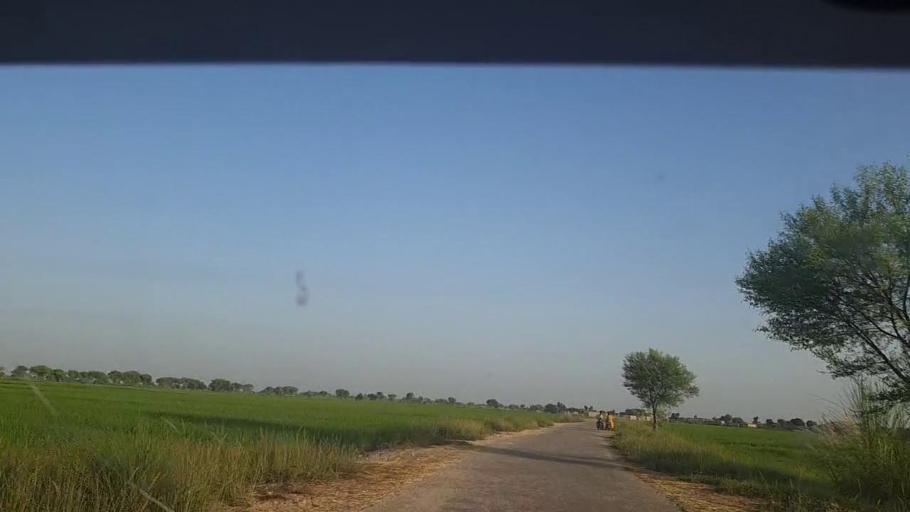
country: PK
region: Sindh
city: Thul
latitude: 28.1350
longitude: 68.8889
